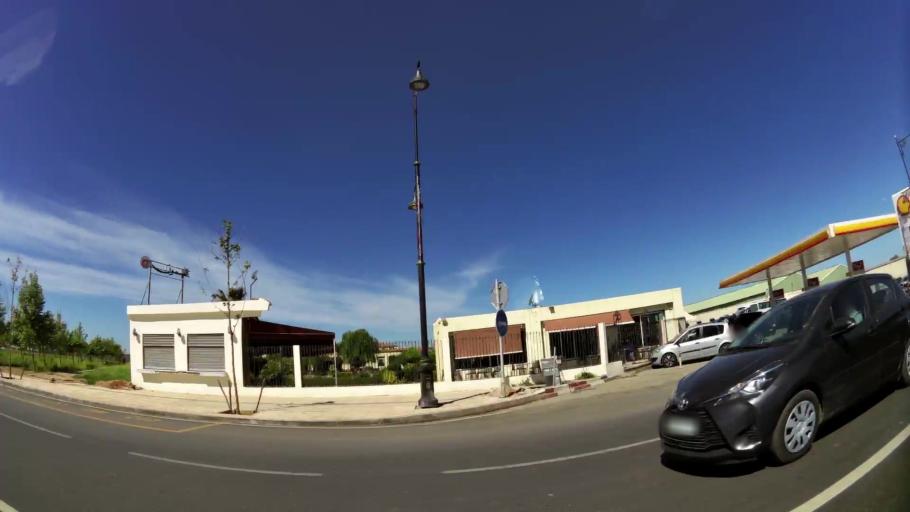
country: MA
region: Meknes-Tafilalet
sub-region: Meknes
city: Meknes
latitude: 33.8457
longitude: -5.5236
